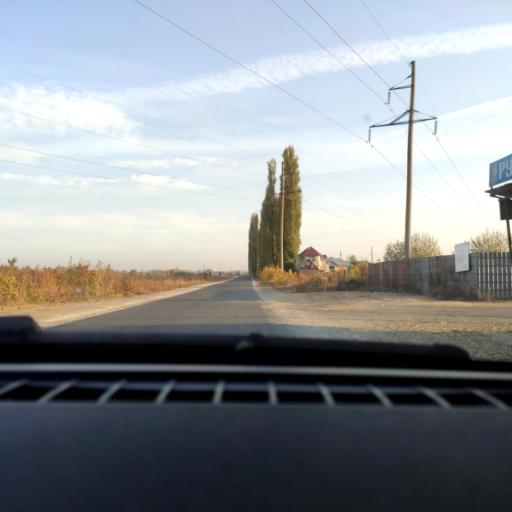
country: RU
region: Voronezj
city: Maslovka
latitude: 51.5233
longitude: 39.2269
